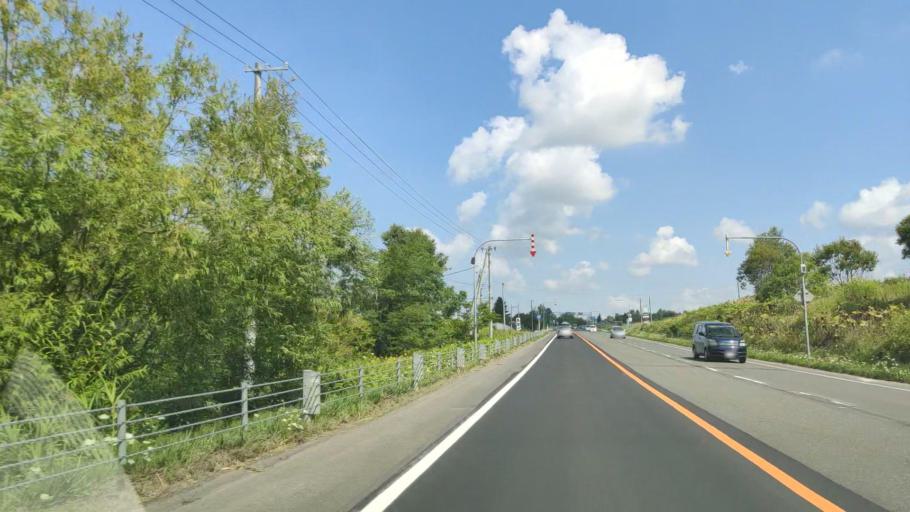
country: JP
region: Hokkaido
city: Shimo-furano
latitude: 43.5381
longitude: 142.4392
